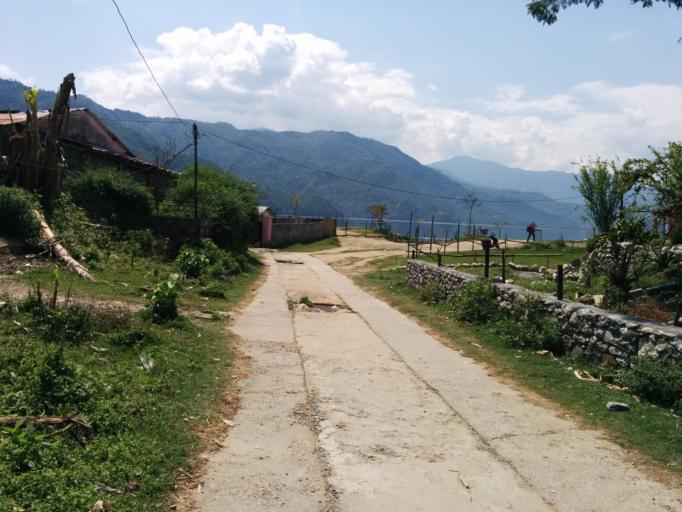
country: NP
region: Western Region
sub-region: Gandaki Zone
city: Pokhara
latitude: 28.2170
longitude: 83.9580
